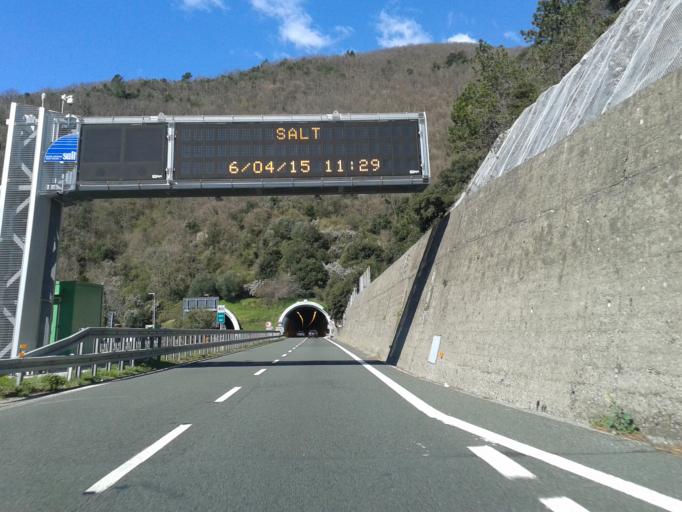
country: IT
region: Liguria
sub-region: Provincia di La Spezia
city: Deiva Marina
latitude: 44.2455
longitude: 9.5399
